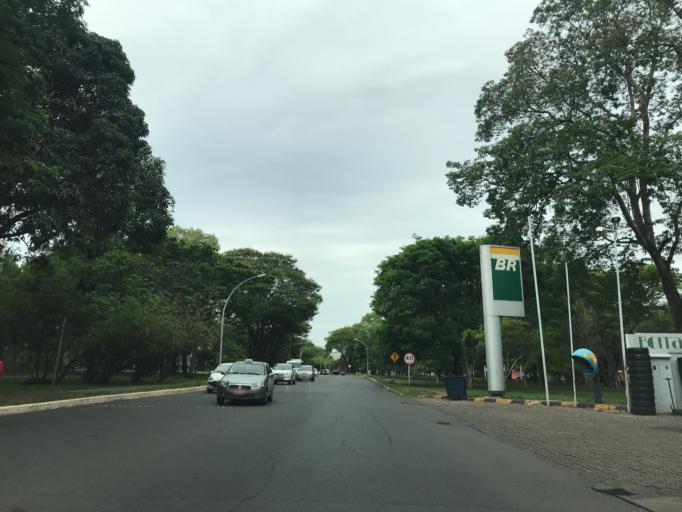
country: BR
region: Federal District
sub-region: Brasilia
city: Brasilia
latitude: -15.8095
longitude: -47.8876
